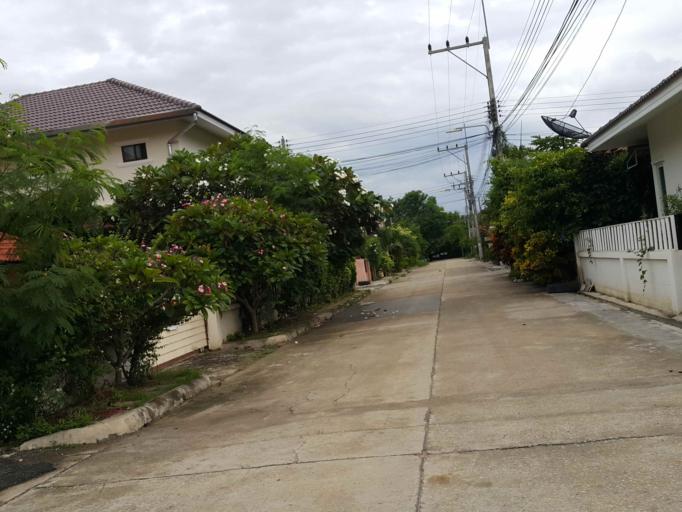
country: TH
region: Chiang Mai
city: San Sai
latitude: 18.8205
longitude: 99.0552
